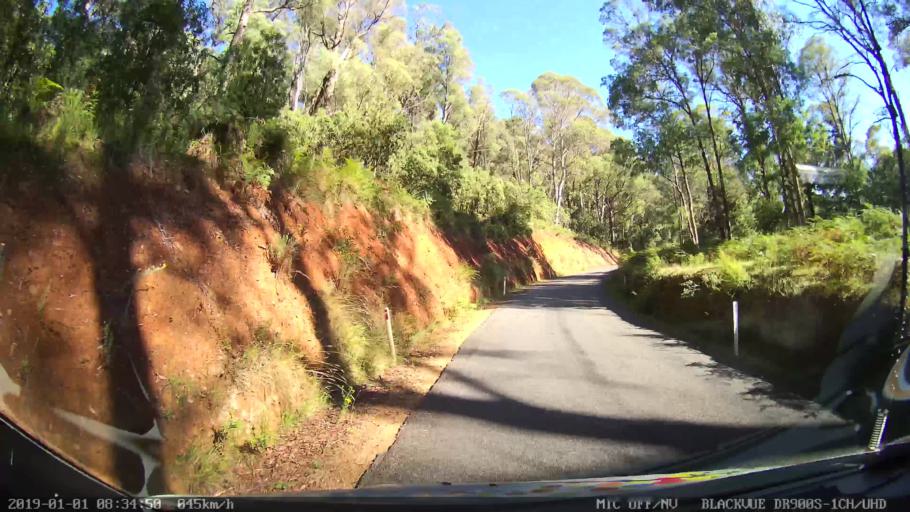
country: AU
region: New South Wales
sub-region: Snowy River
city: Jindabyne
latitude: -36.3527
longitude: 148.1931
